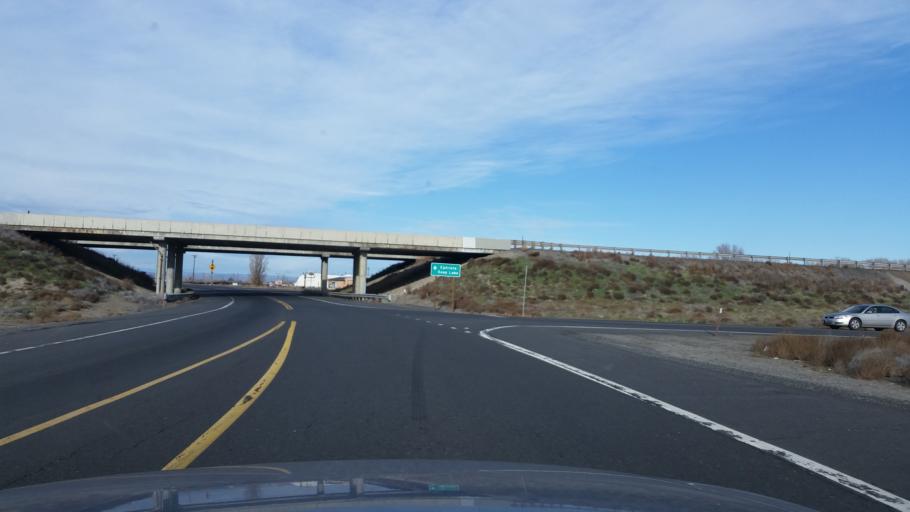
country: US
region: Washington
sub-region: Grant County
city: Quincy
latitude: 47.1018
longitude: -119.8289
